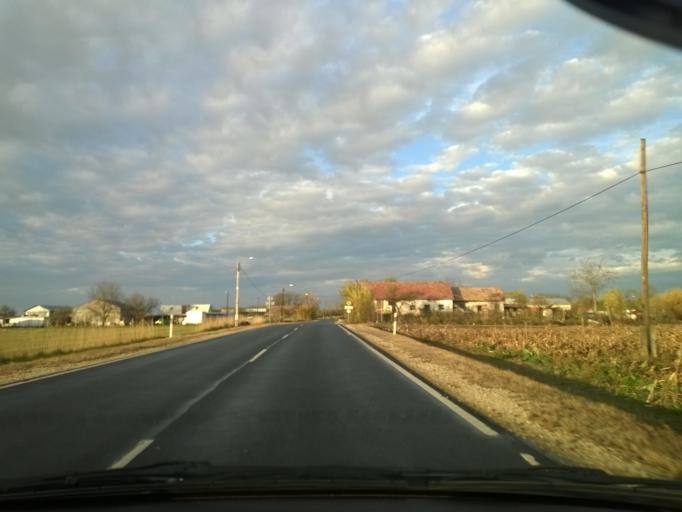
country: HU
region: Bacs-Kiskun
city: Kalocsa
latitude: 46.5739
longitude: 18.9749
